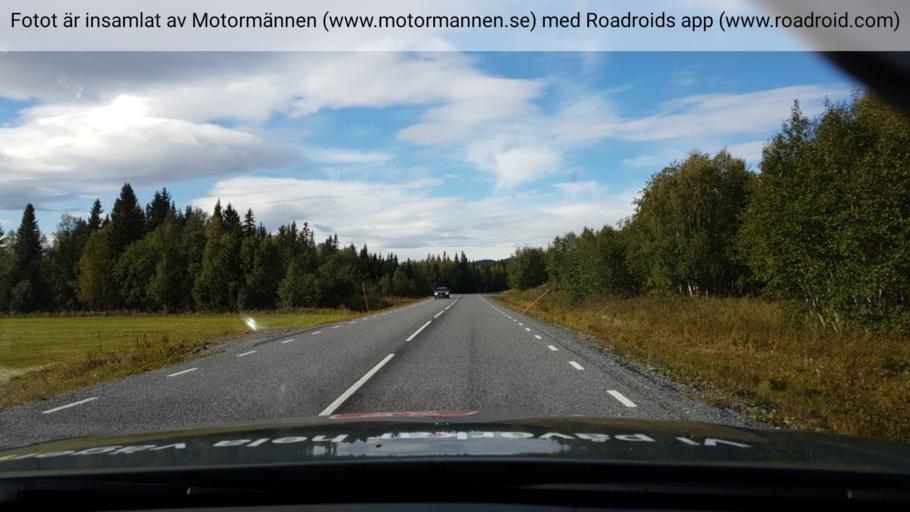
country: SE
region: Jaemtland
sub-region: Are Kommun
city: Are
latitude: 63.4499
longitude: 12.6701
